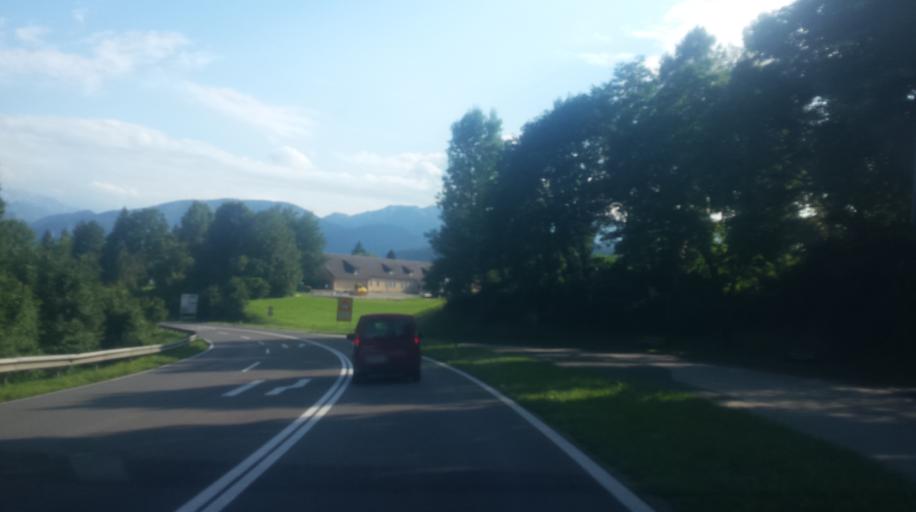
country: AT
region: Upper Austria
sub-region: Politischer Bezirk Gmunden
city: Altmunster
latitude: 47.9159
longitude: 13.7770
